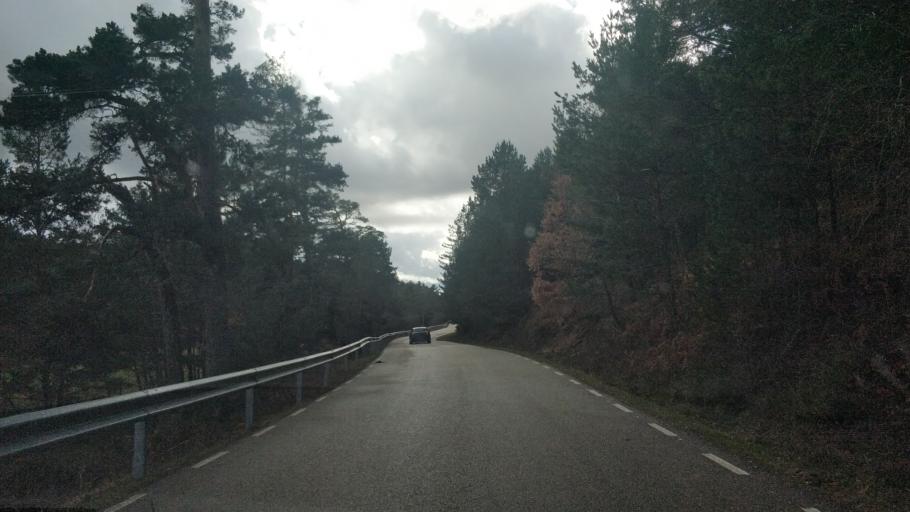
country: ES
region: Castille and Leon
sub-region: Provincia de Burgos
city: Neila
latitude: 42.0276
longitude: -3.0107
